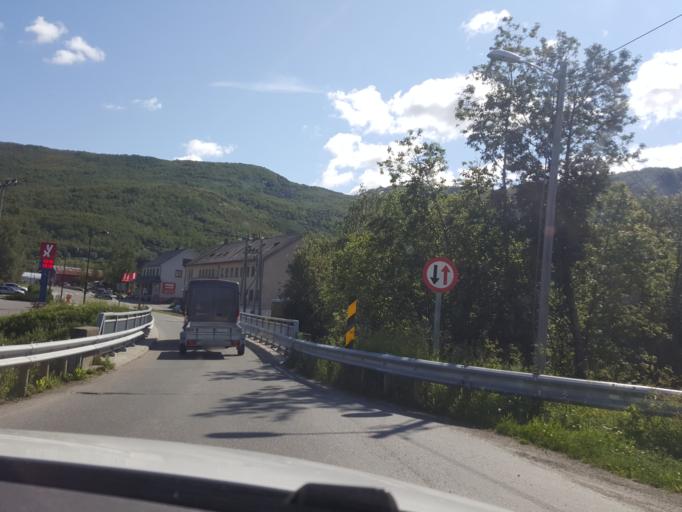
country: NO
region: Nordland
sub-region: Bodo
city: Loding
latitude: 67.1165
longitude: 15.0033
